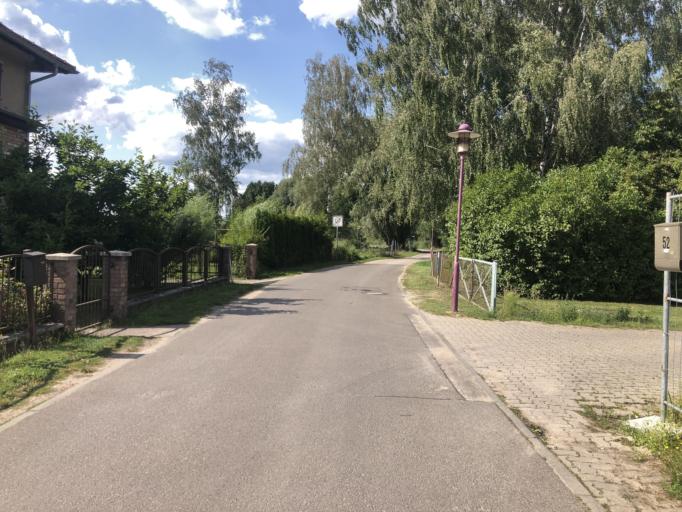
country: DE
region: Brandenburg
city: Mullrose
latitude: 52.2494
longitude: 14.4107
